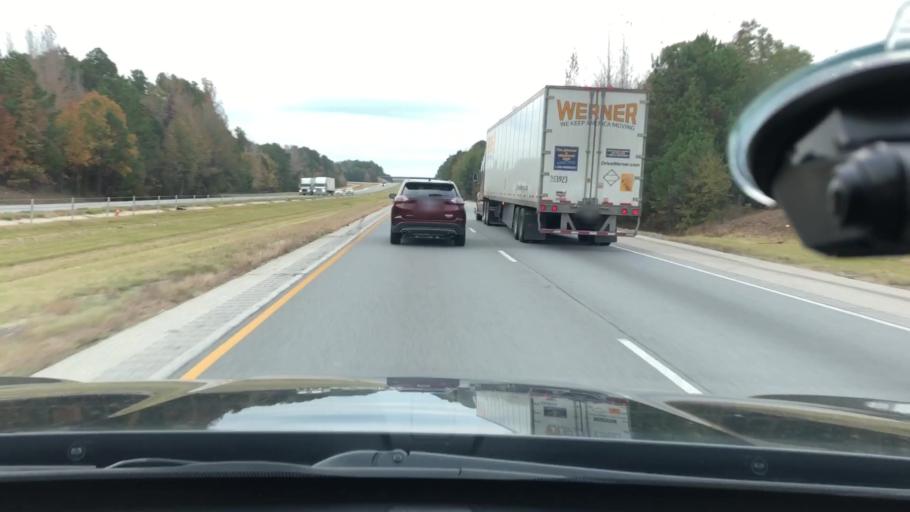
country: US
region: Arkansas
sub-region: Clark County
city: Arkadelphia
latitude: 34.0657
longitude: -93.1248
